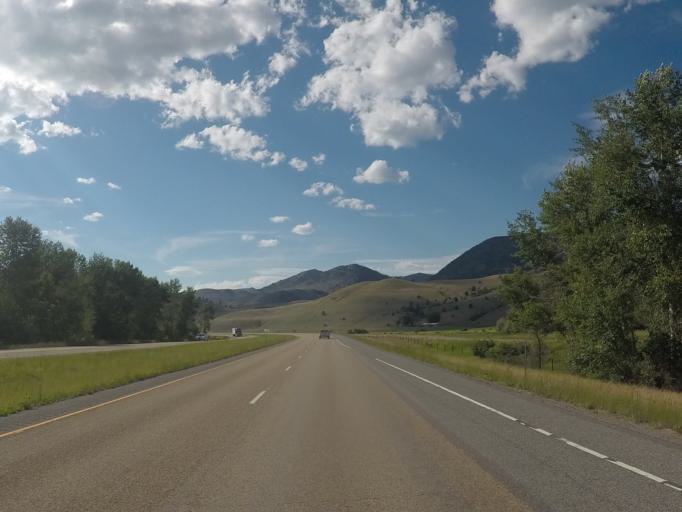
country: US
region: Montana
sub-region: Granite County
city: Philipsburg
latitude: 46.6942
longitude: -113.2045
